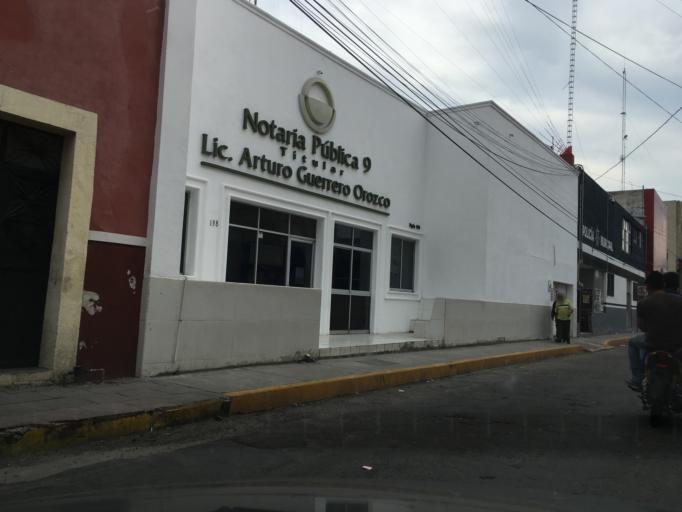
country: MX
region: Guanajuato
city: Celaya
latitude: 20.5182
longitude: -100.8155
